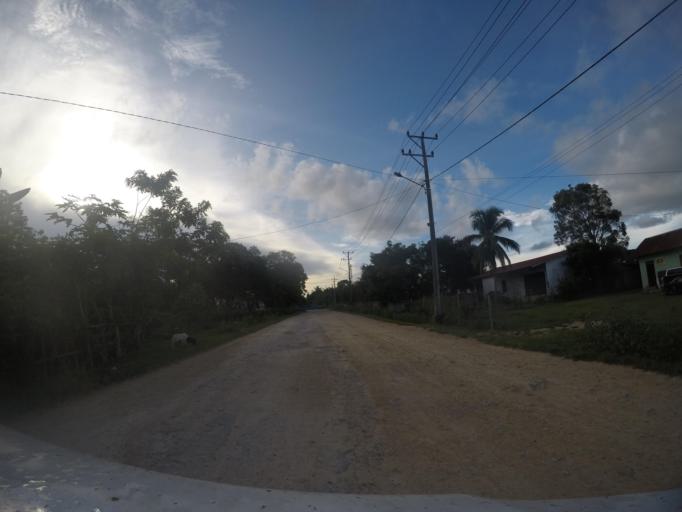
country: TL
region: Lautem
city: Lospalos
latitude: -8.4965
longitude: 126.9933
